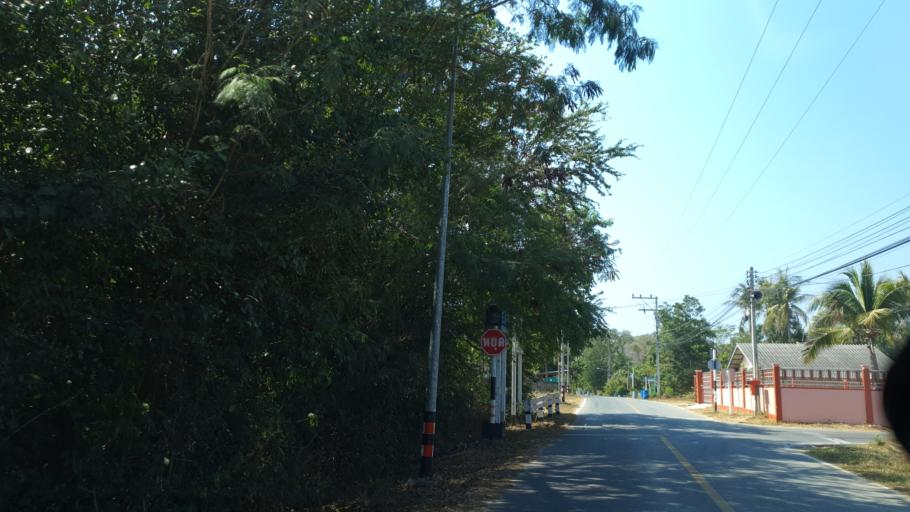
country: TH
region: Prachuap Khiri Khan
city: Sam Roi Yot
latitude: 12.2770
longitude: 99.9733
